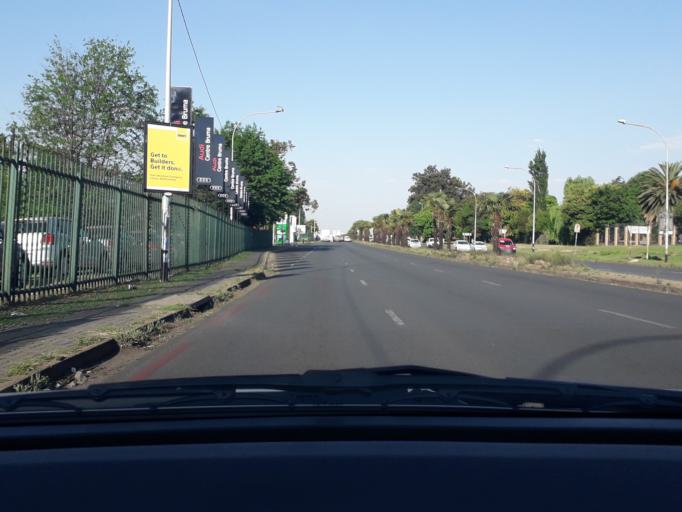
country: ZA
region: Gauteng
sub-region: City of Johannesburg Metropolitan Municipality
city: Johannesburg
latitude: -26.1837
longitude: 28.1060
